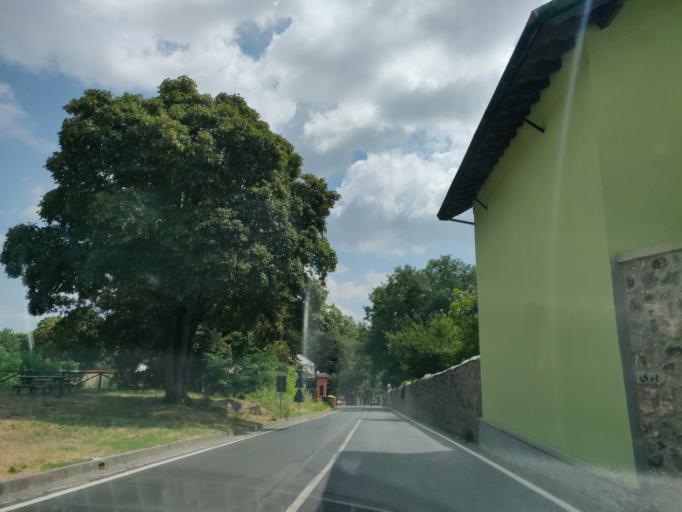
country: IT
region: Tuscany
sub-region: Provincia di Siena
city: Abbadia San Salvatore
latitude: 42.8832
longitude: 11.6650
